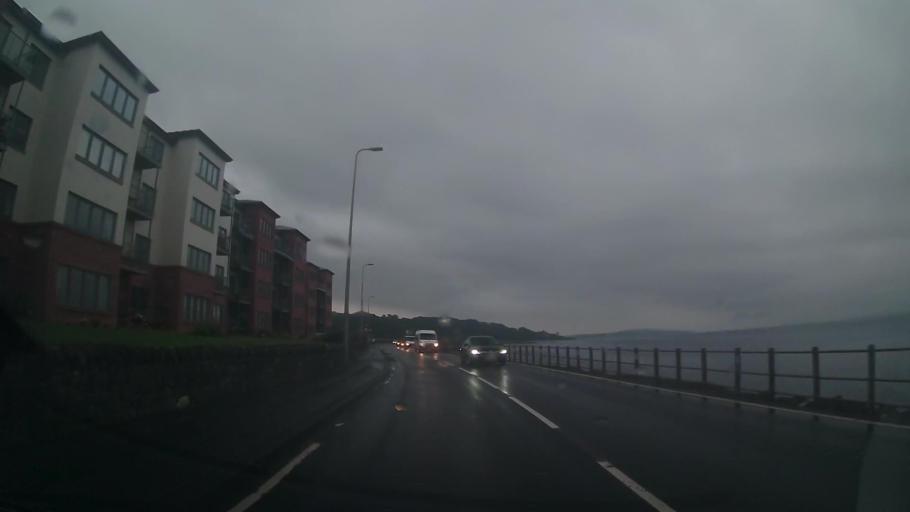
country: GB
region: Scotland
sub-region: North Ayrshire
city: Skelmorlie
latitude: 55.8561
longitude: -4.8900
